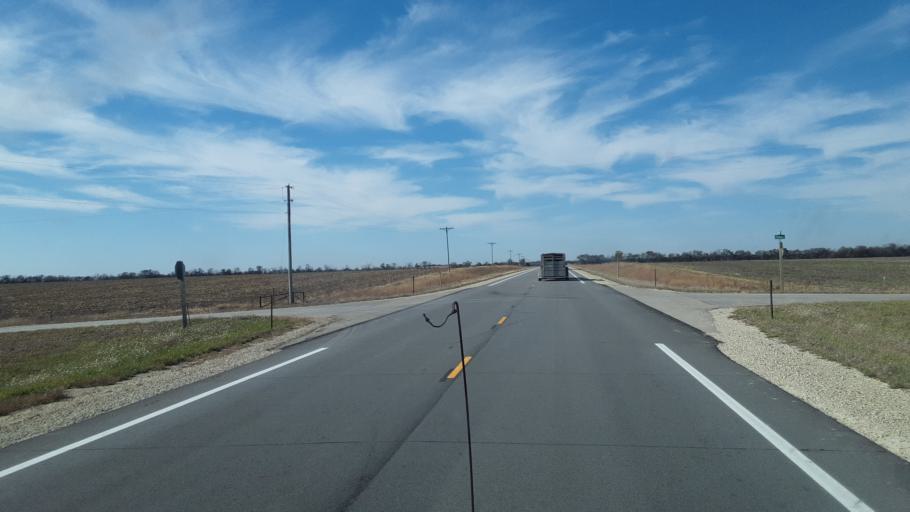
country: US
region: Kansas
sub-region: Marion County
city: Marion
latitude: 38.3630
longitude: -96.8925
